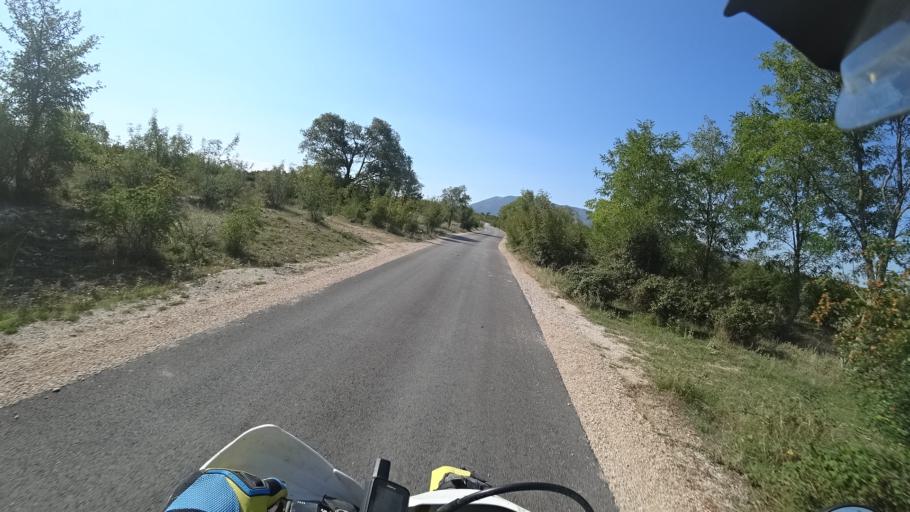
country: HR
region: Sibensko-Kniniska
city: Knin
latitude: 44.0017
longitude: 16.1941
